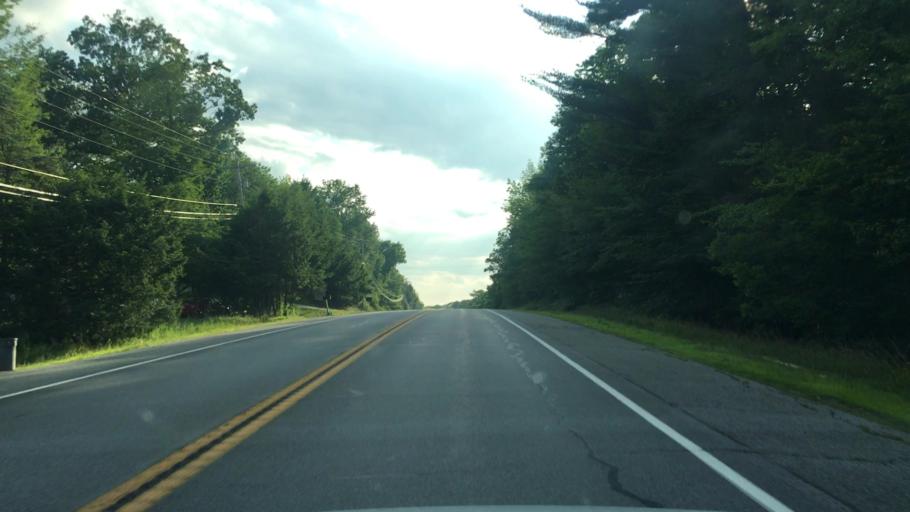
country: US
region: Maine
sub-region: Kennebec County
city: Sidney
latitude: 44.3349
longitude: -69.6966
